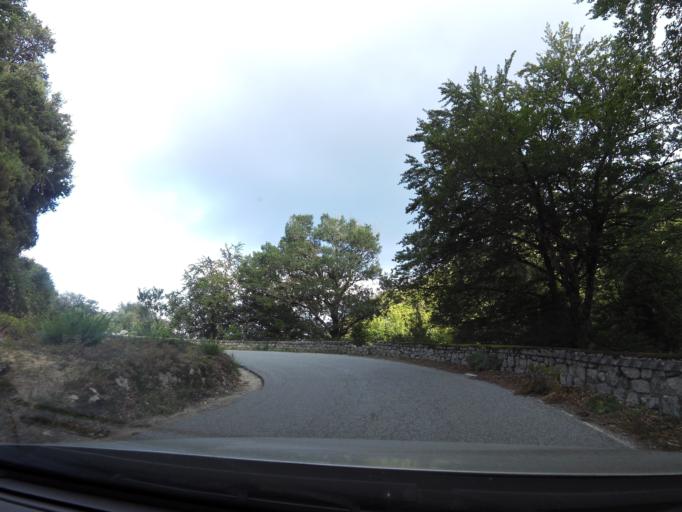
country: IT
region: Calabria
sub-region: Provincia di Vibo-Valentia
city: Nardodipace
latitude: 38.4818
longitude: 16.3787
